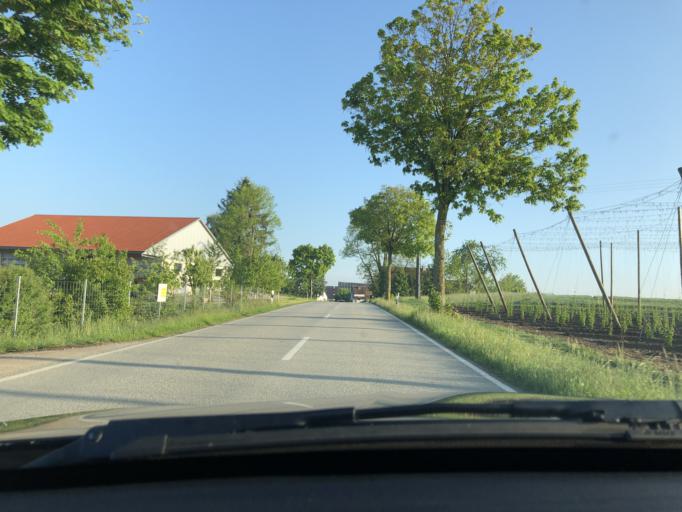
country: DE
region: Bavaria
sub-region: Upper Bavaria
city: Schweitenkirchen
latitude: 48.4839
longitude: 11.6293
